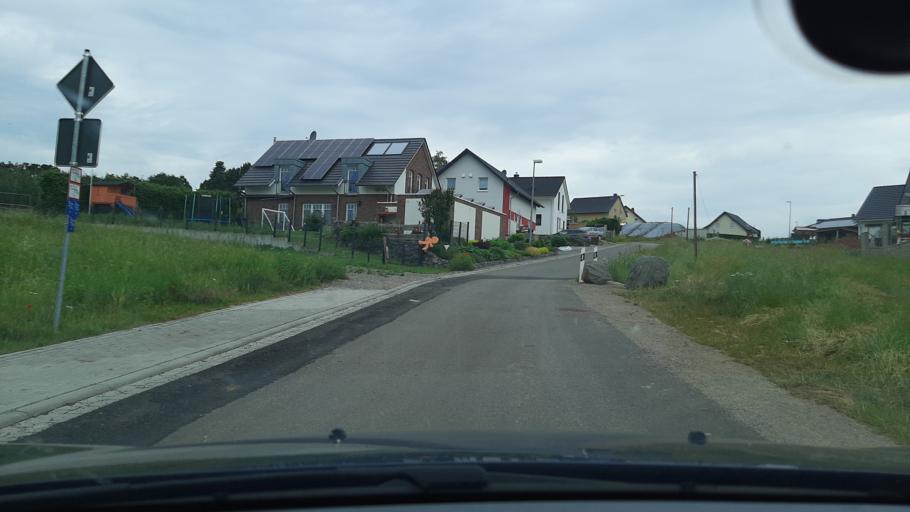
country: DE
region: North Rhine-Westphalia
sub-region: Regierungsbezirk Koln
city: Mechernich
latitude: 50.5875
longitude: 6.6711
